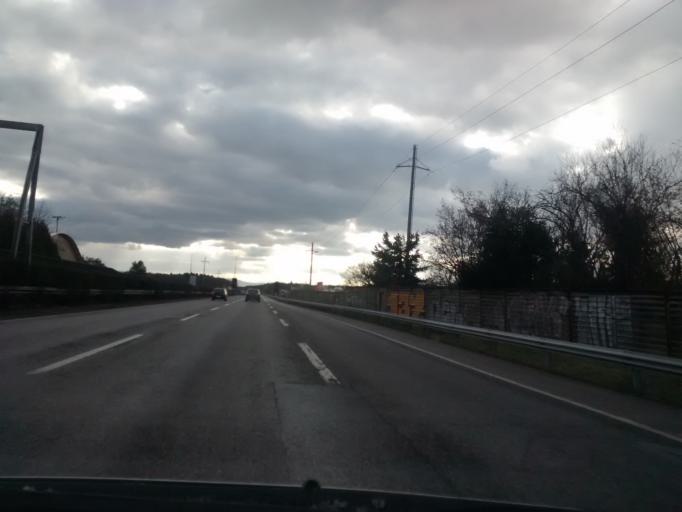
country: CH
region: Vaud
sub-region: Nyon District
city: Founex
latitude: 46.3366
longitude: 6.1606
